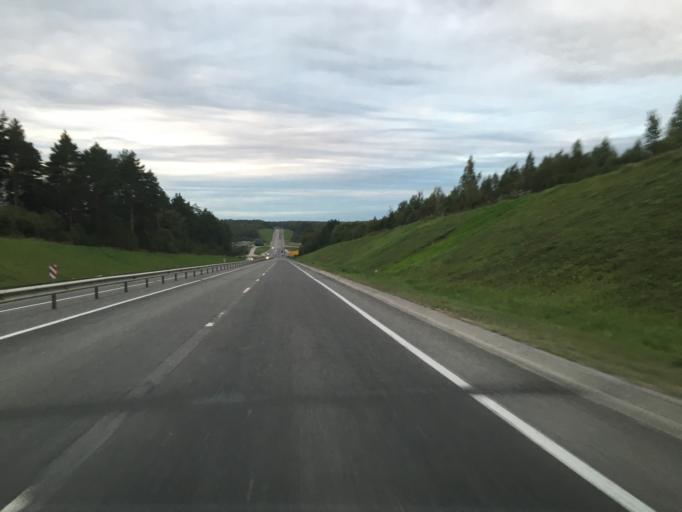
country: RU
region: Kaluga
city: Kaluga
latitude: 54.5942
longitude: 36.3260
